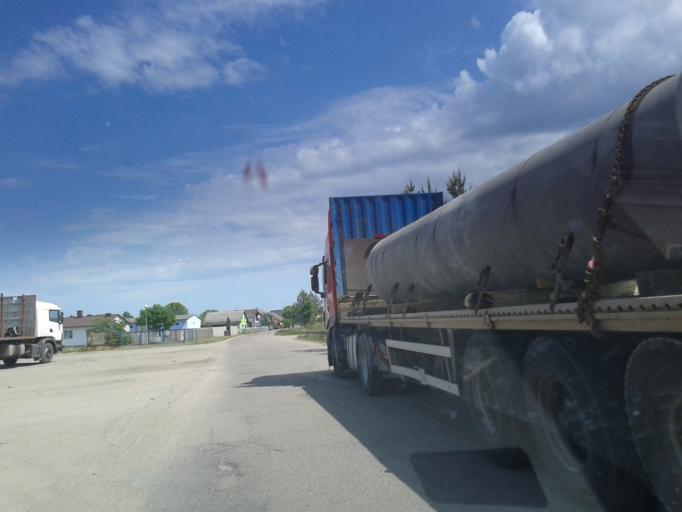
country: PL
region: Pomeranian Voivodeship
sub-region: Powiat koscierski
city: Karsin
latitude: 53.8946
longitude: 17.9259
